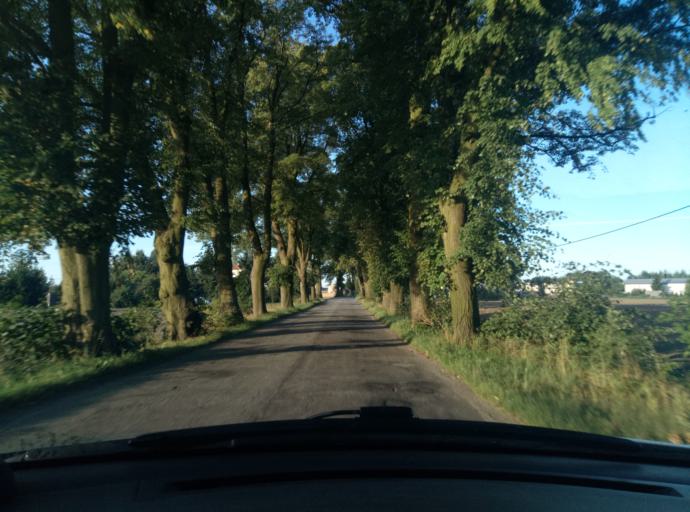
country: PL
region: Kujawsko-Pomorskie
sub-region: Powiat brodnicki
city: Jablonowo Pomorskie
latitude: 53.4020
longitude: 19.1683
